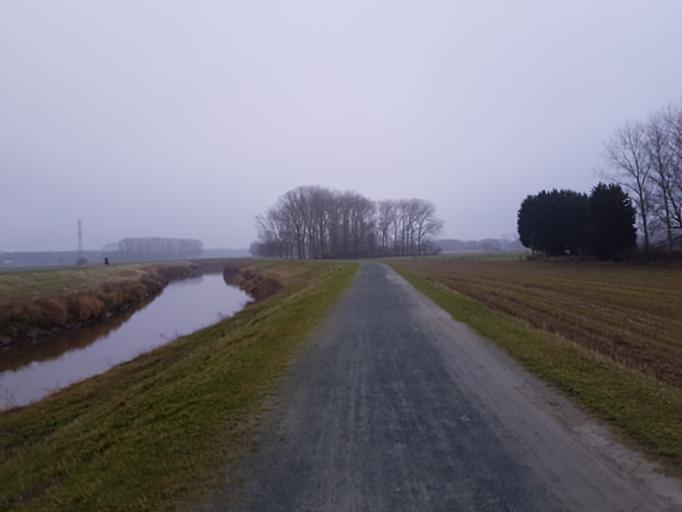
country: BE
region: Flanders
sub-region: Provincie Vlaams-Brabant
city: Keerbergen
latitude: 50.9932
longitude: 4.6199
